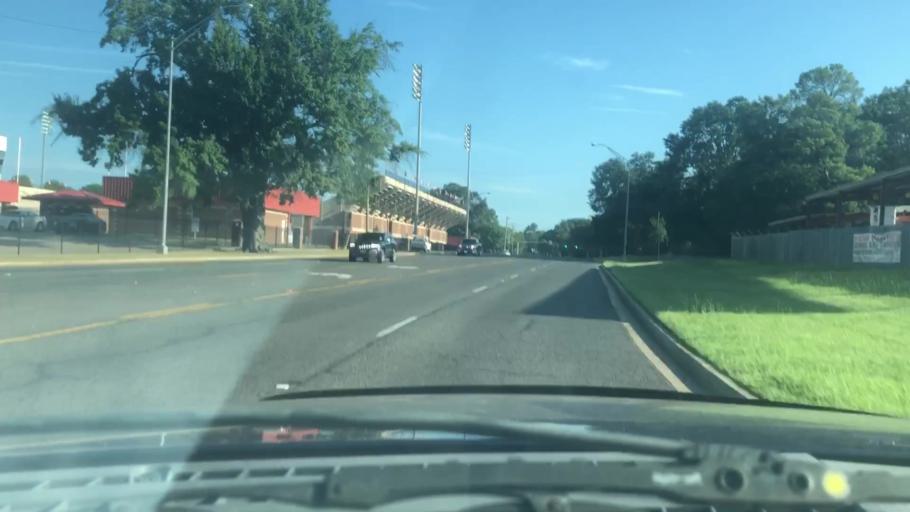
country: US
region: Texas
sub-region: Bowie County
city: Texarkana
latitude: 33.4266
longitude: -94.0614
